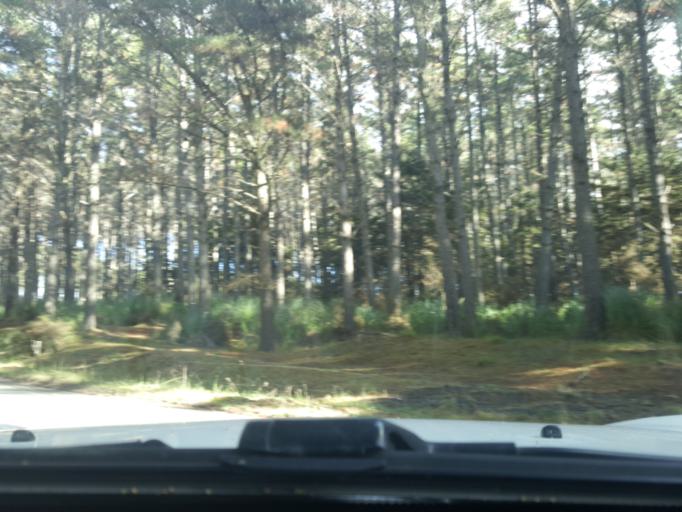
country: NZ
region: Auckland
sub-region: Auckland
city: Muriwai Beach
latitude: -36.7407
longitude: 174.4223
